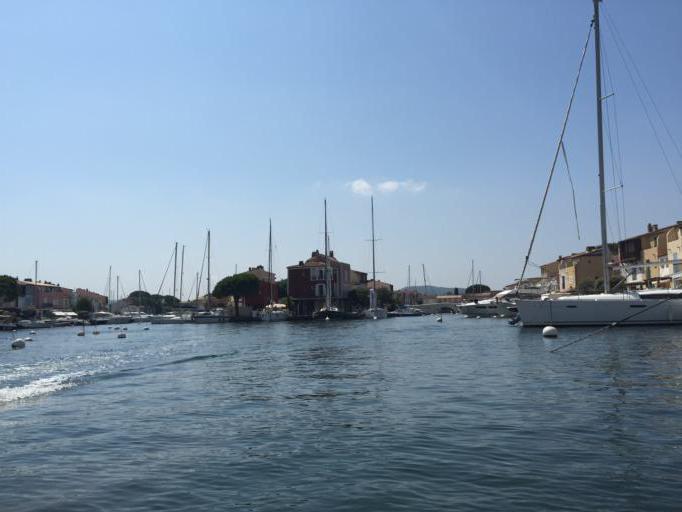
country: FR
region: Provence-Alpes-Cote d'Azur
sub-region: Departement du Var
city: Gassin
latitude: 43.2742
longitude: 6.5789
